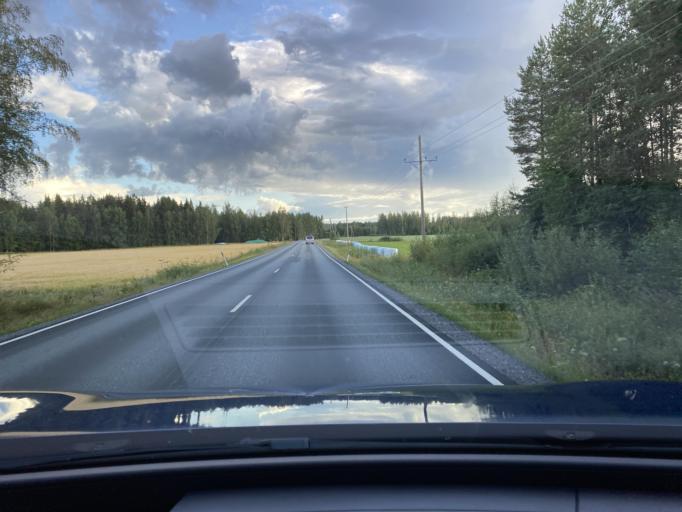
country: FI
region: Southern Ostrobothnia
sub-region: Seinaejoki
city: Jalasjaervi
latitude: 62.5144
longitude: 22.6564
